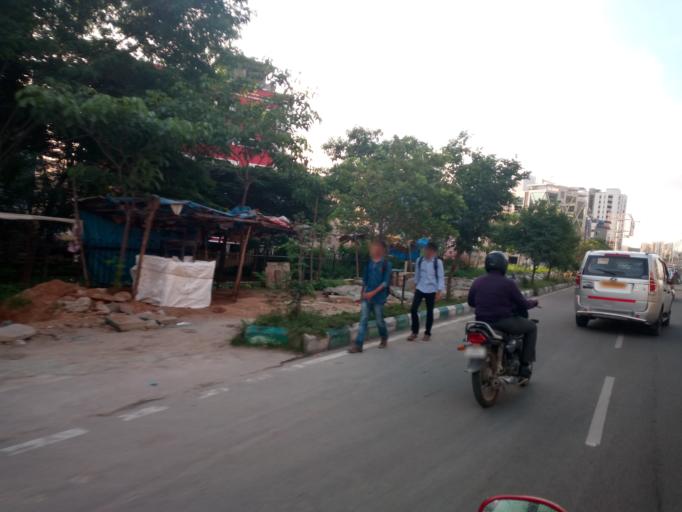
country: IN
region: Telangana
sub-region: Rangareddi
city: Kukatpalli
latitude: 17.4312
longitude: 78.3750
